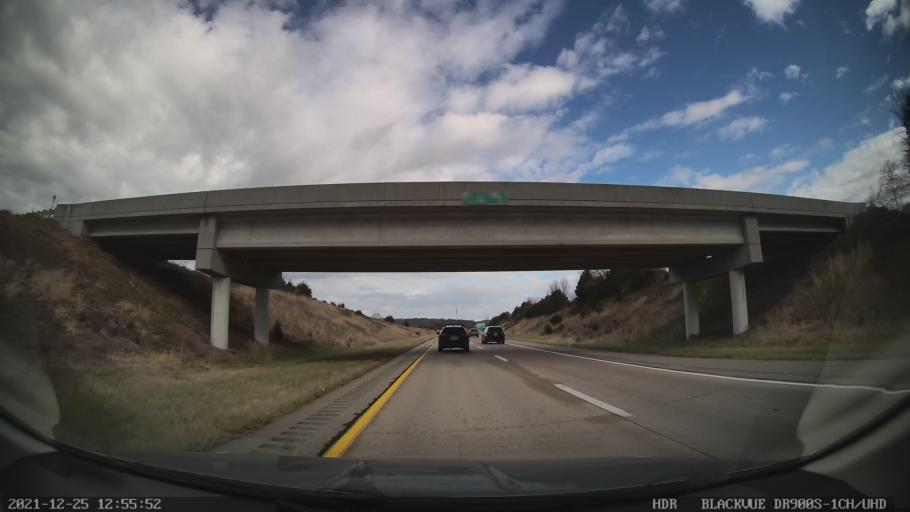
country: US
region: Pennsylvania
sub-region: Adams County
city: Lake Heritage
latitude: 39.7863
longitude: -77.2170
